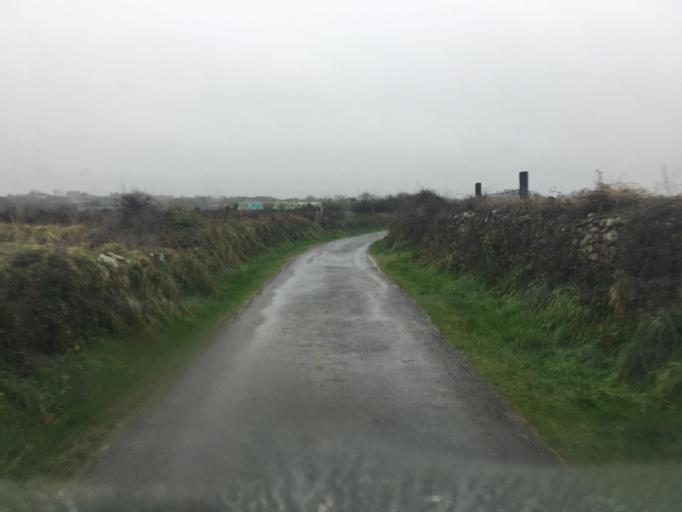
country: FR
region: Lower Normandy
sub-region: Departement de la Manche
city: Beaumont-Hague
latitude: 49.7190
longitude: -1.9202
